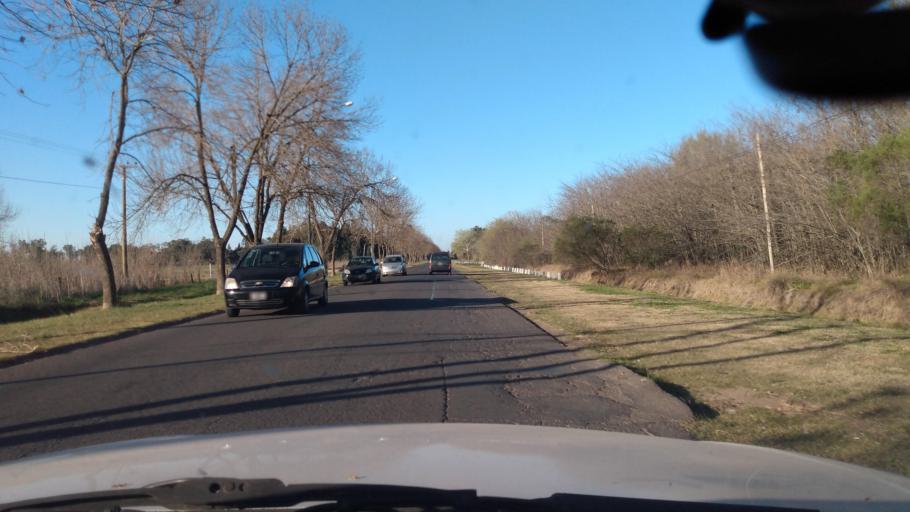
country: AR
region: Buenos Aires
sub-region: Partido de Lujan
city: Lujan
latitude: -34.5771
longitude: -59.1663
